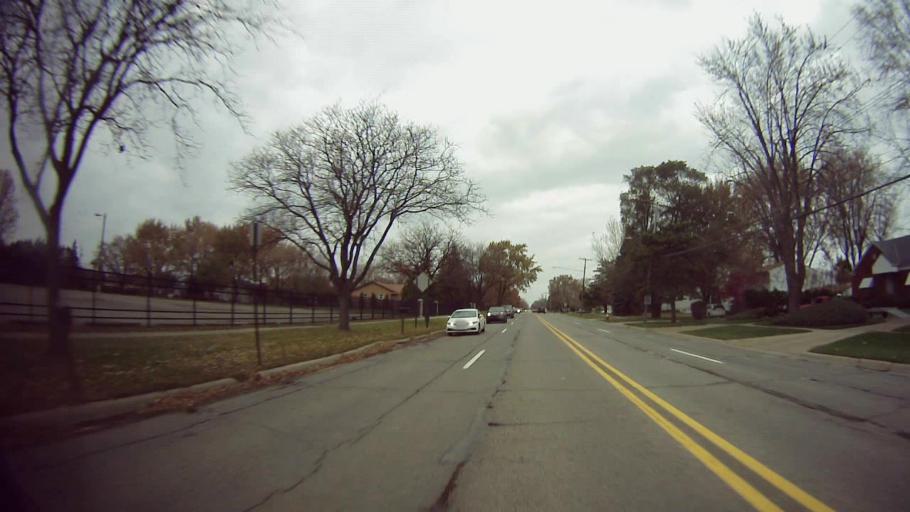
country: US
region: Michigan
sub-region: Macomb County
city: Eastpointe
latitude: 42.4941
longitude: -82.9775
